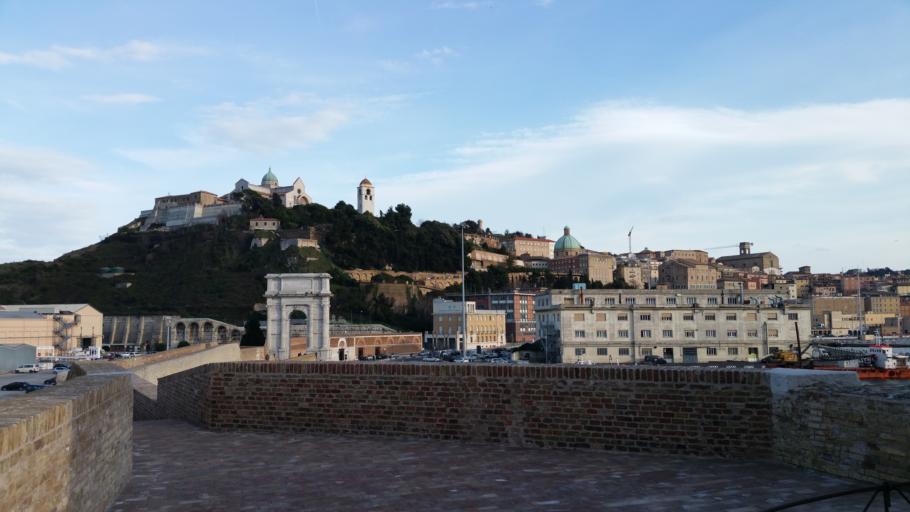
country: IT
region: The Marches
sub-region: Provincia di Ancona
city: Le Grazie di Ancona
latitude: 43.6253
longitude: 13.5049
